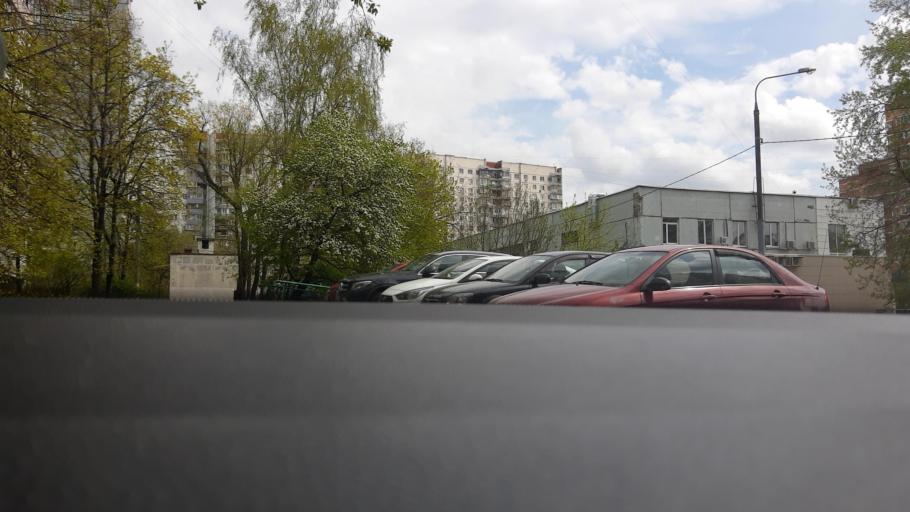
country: RU
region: Moscow
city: Ivanovskoye
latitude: 55.7788
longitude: 37.8260
